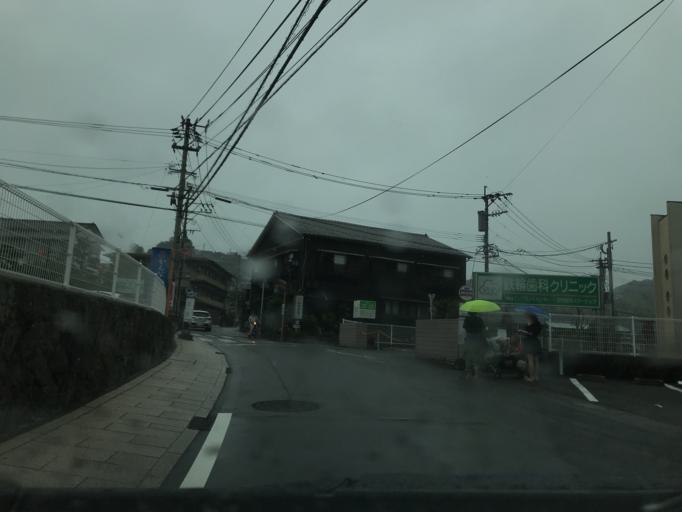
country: JP
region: Oita
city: Beppu
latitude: 33.3153
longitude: 131.4795
